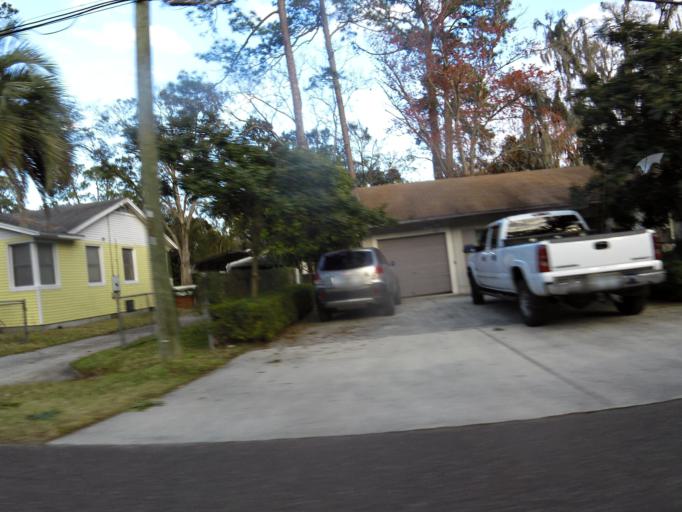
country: US
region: Florida
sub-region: Duval County
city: Jacksonville
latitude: 30.3043
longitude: -81.7262
